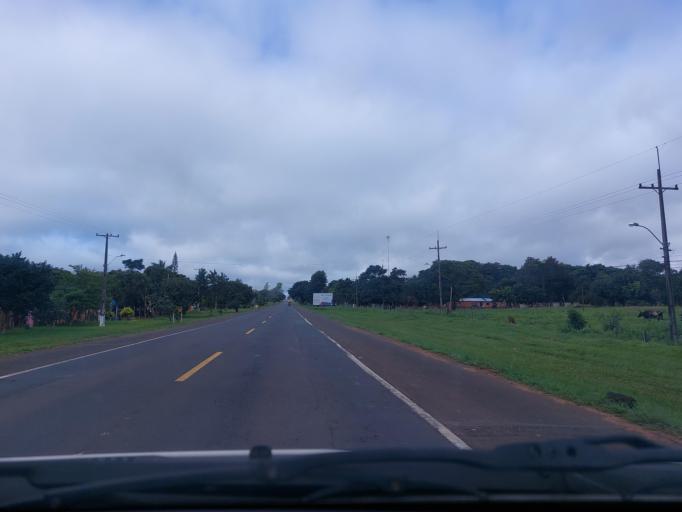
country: PY
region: San Pedro
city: Guayaybi
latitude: -24.5592
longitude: -56.4035
